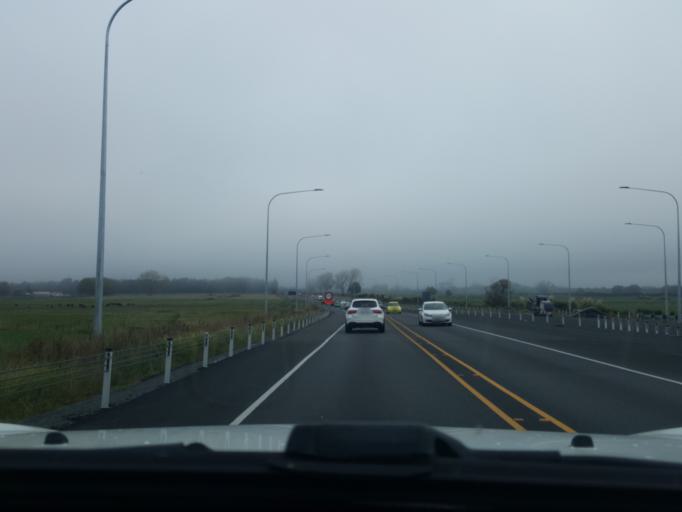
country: NZ
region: Waikato
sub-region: Waikato District
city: Te Kauwhata
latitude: -37.5059
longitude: 175.1654
